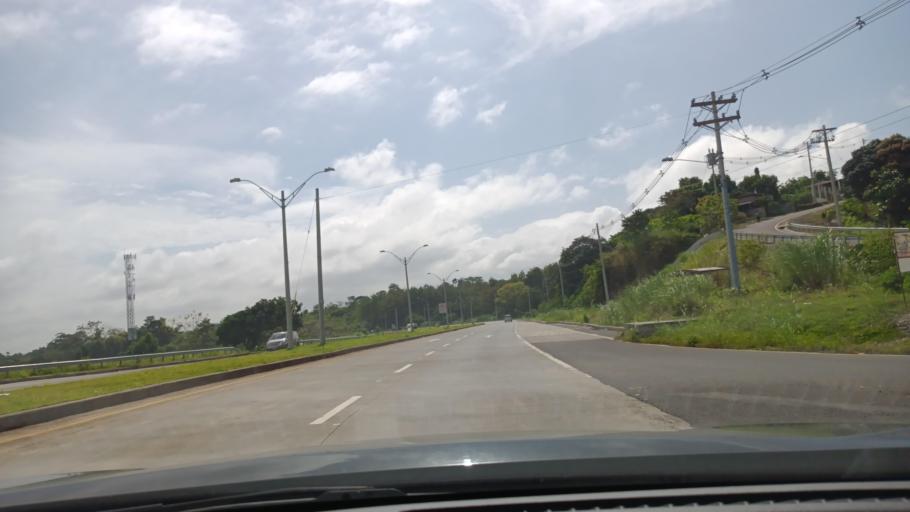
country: PA
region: Panama
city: Las Cumbres
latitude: 9.0989
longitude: -79.4884
